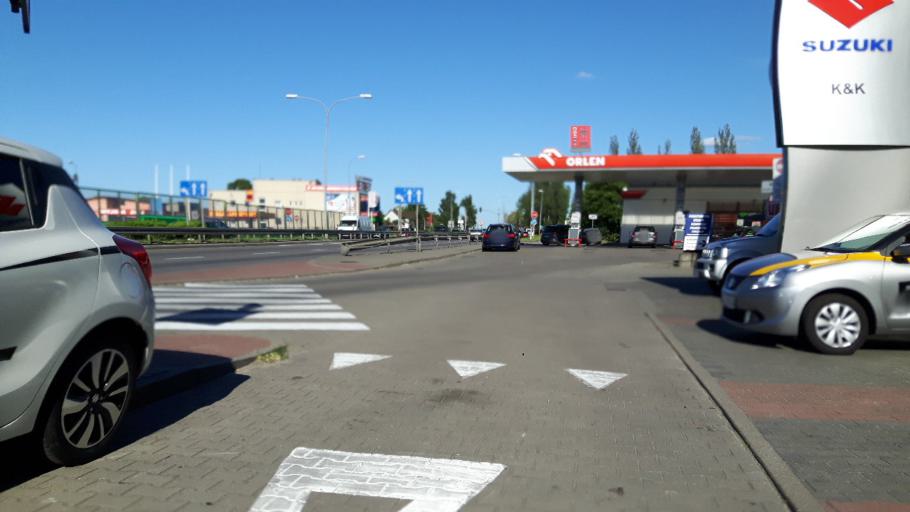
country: PL
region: Pomeranian Voivodeship
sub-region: Powiat wejherowski
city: Wejherowo
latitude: 54.6027
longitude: 18.2708
